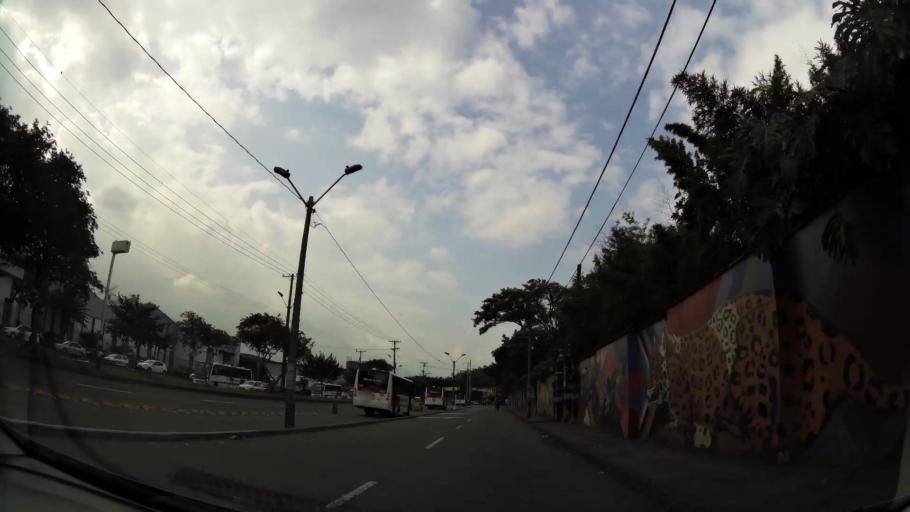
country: CO
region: Antioquia
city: Medellin
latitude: 6.2226
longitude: -75.5797
